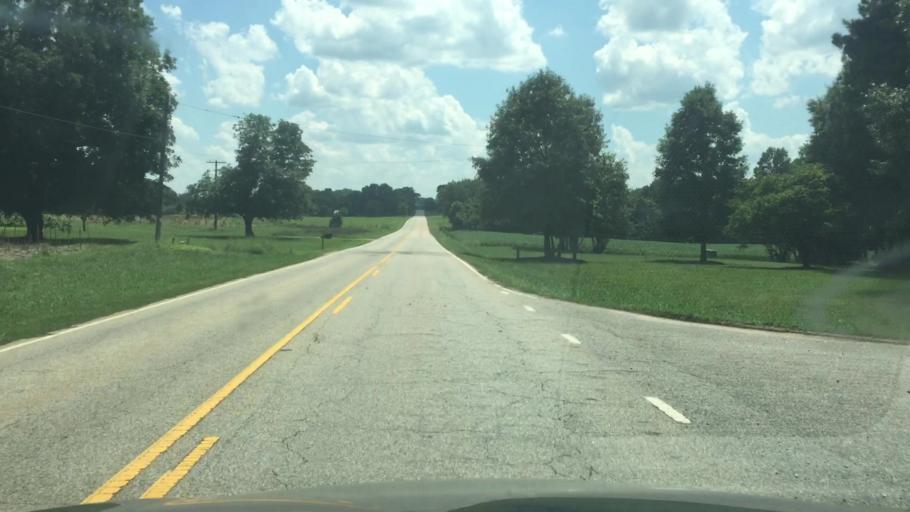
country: US
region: North Carolina
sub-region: Rowan County
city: China Grove
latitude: 35.6374
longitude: -80.6404
